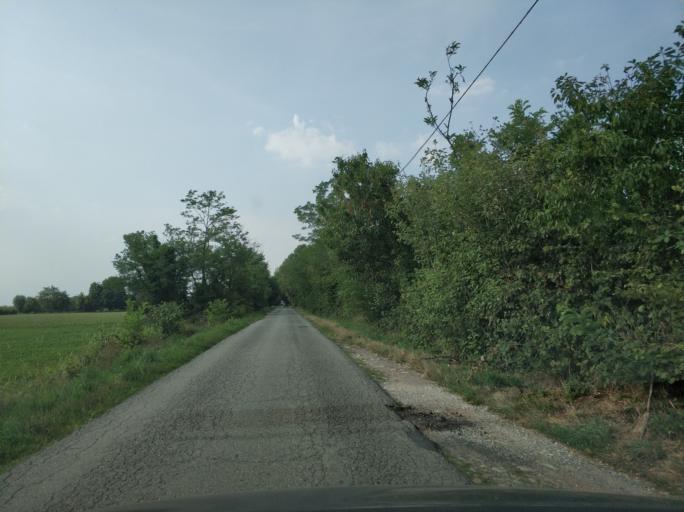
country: IT
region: Piedmont
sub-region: Provincia di Torino
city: Leini
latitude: 45.1853
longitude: 7.6875
